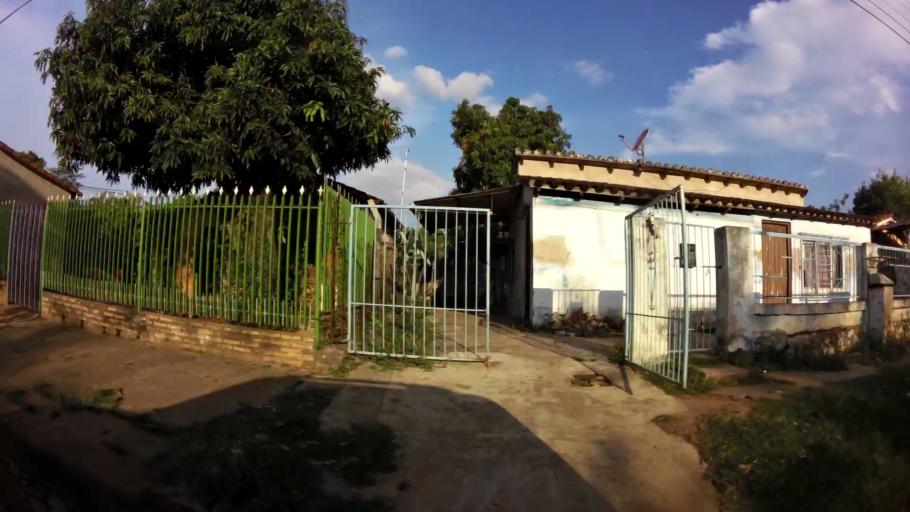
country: PY
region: Central
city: Fernando de la Mora
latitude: -25.3515
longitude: -57.5275
